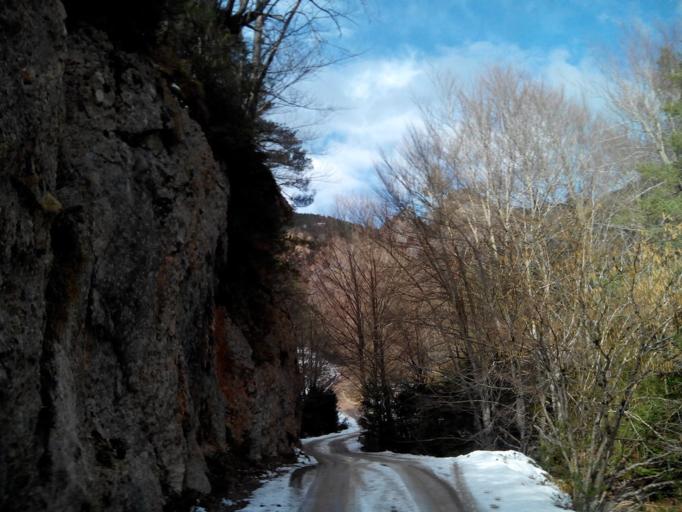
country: ES
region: Catalonia
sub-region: Provincia de Barcelona
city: Vilada
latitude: 42.1779
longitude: 1.9285
